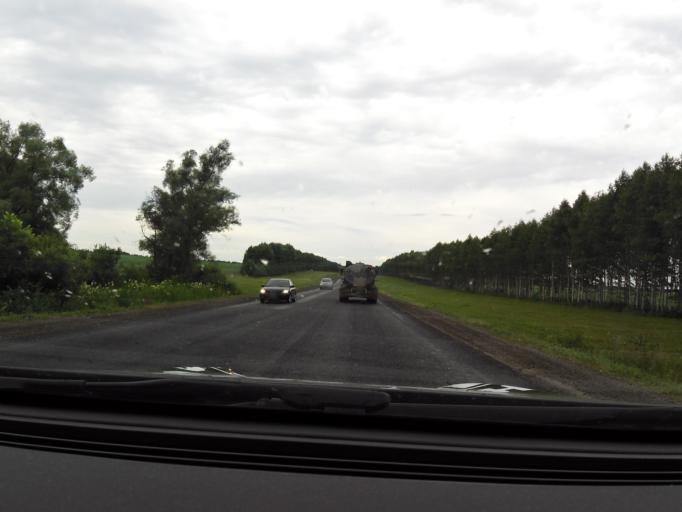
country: RU
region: Bashkortostan
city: Iglino
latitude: 54.7743
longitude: 56.4751
